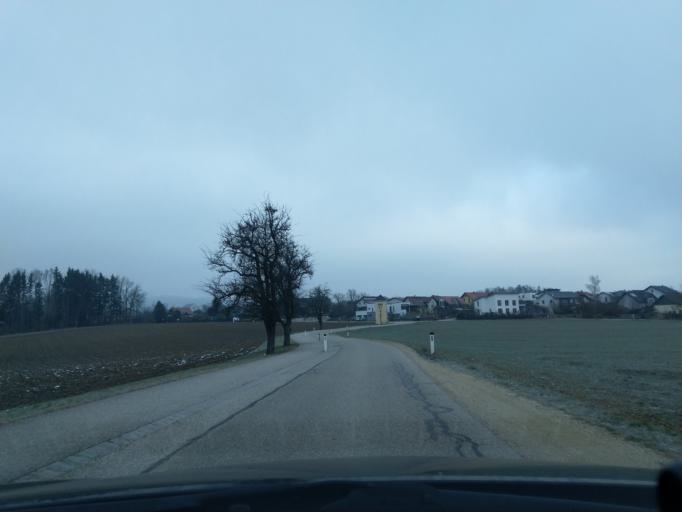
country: AT
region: Upper Austria
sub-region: Politischer Bezirk Urfahr-Umgebung
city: Engerwitzdorf
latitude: 48.3702
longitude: 14.5214
